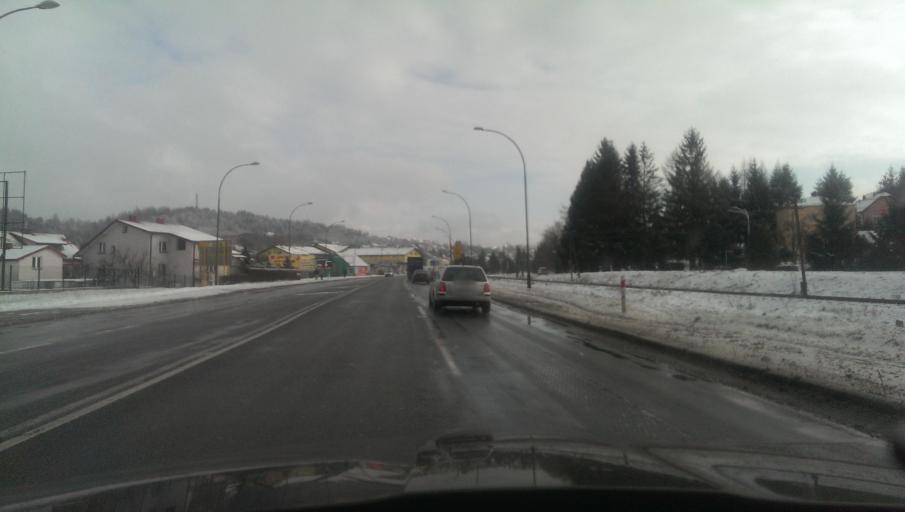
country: PL
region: Subcarpathian Voivodeship
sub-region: Powiat sanocki
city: Sanok
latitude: 49.5694
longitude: 22.1612
